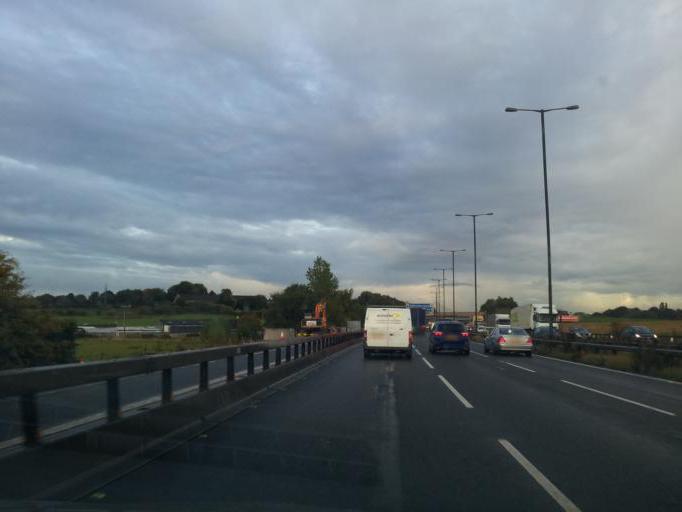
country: GB
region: England
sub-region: Manchester
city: Heywood
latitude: 53.5618
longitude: -2.2425
